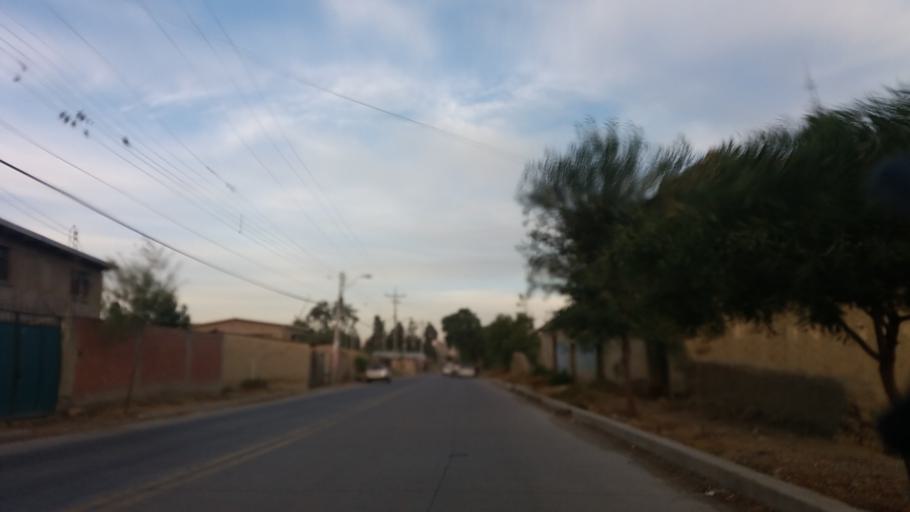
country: BO
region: Cochabamba
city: Cochabamba
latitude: -17.3711
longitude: -66.2051
